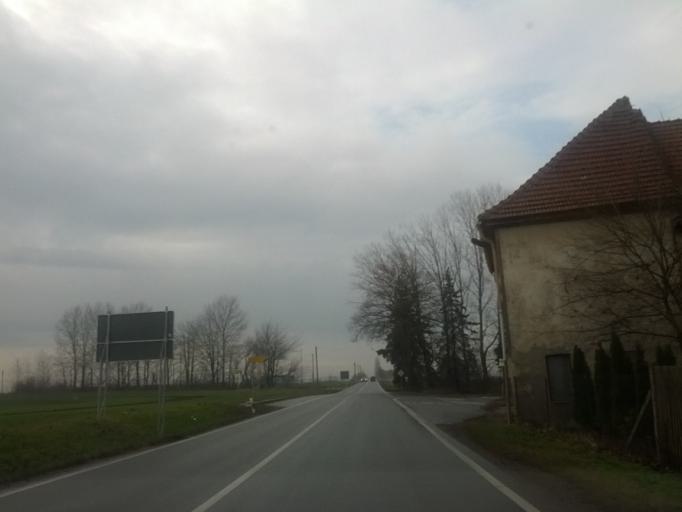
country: DE
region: Thuringia
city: Bufleben
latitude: 50.9759
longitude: 10.7492
